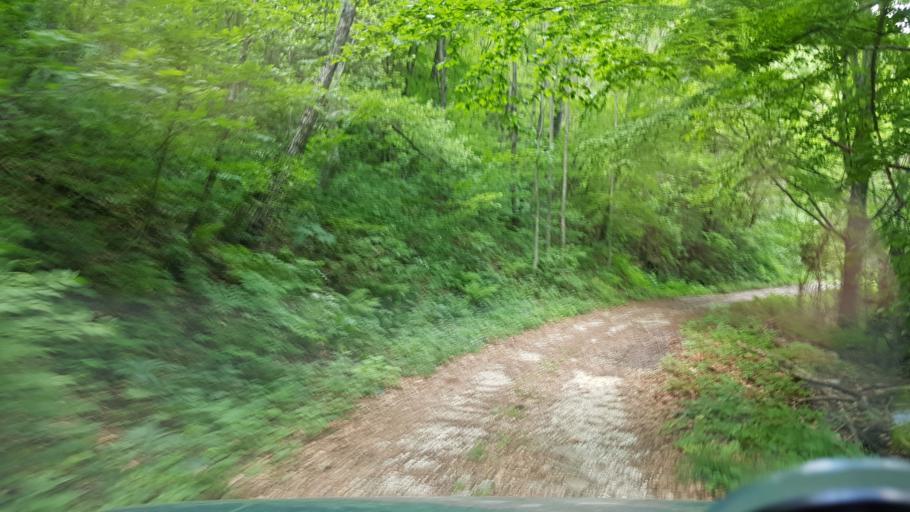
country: IT
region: Friuli Venezia Giulia
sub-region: Provincia di Udine
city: Torreano
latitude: 46.1865
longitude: 13.4221
